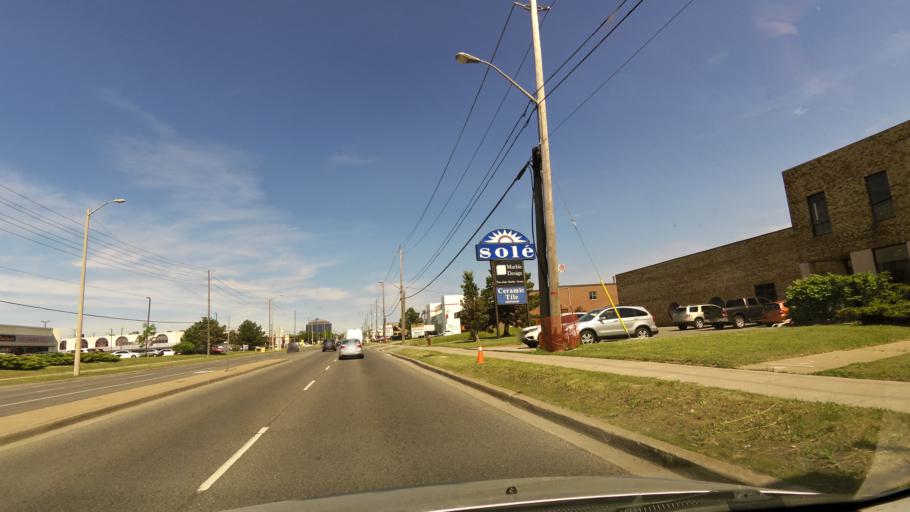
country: CA
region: Ontario
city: Concord
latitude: 43.7685
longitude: -79.5548
